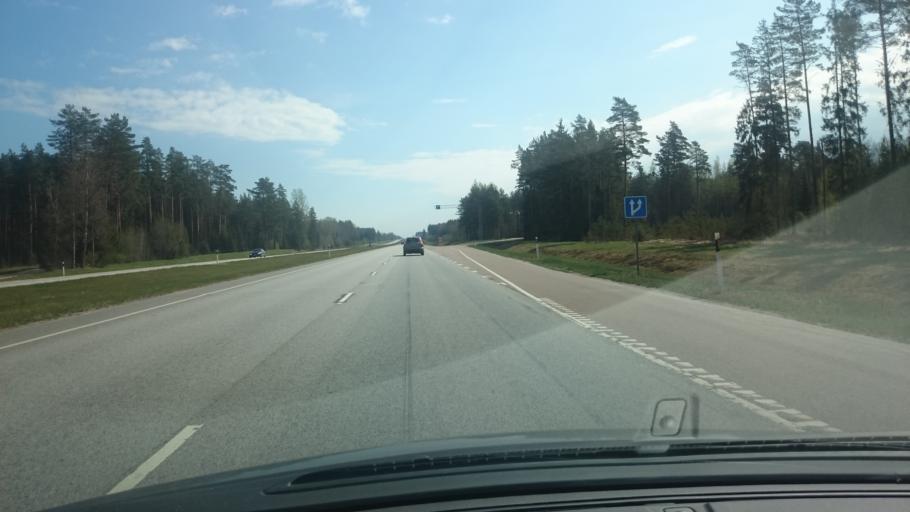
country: EE
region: Harju
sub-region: Raasiku vald
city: Raasiku
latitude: 59.4375
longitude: 25.2407
